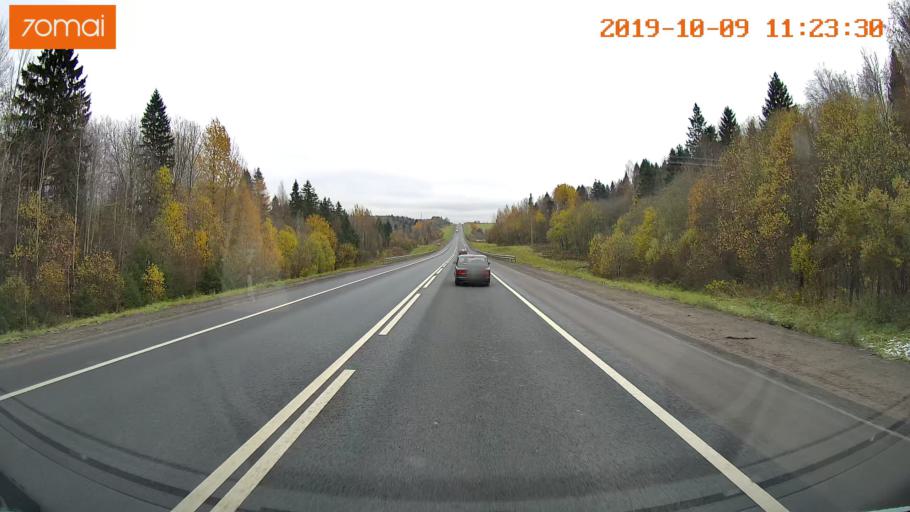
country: RU
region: Vologda
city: Vologda
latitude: 59.1205
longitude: 39.9701
